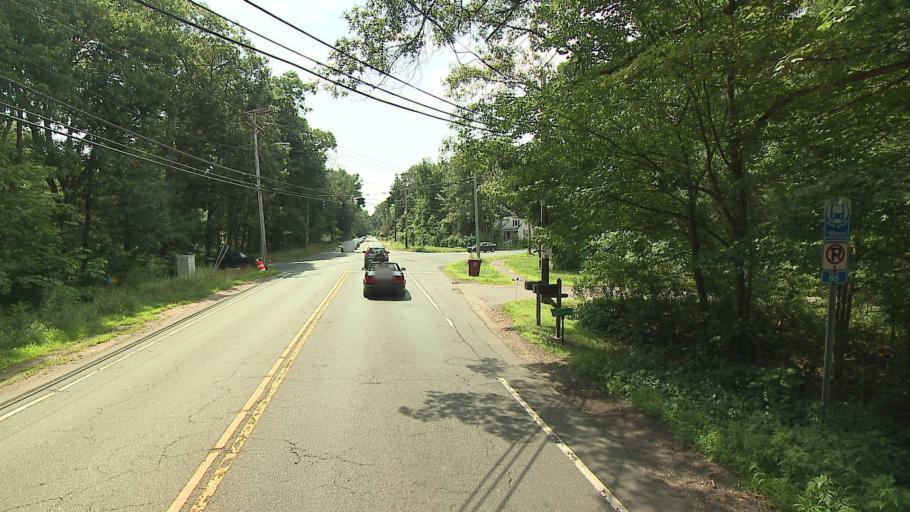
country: US
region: Connecticut
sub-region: Hartford County
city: Farmington
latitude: 41.7370
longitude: -72.8910
